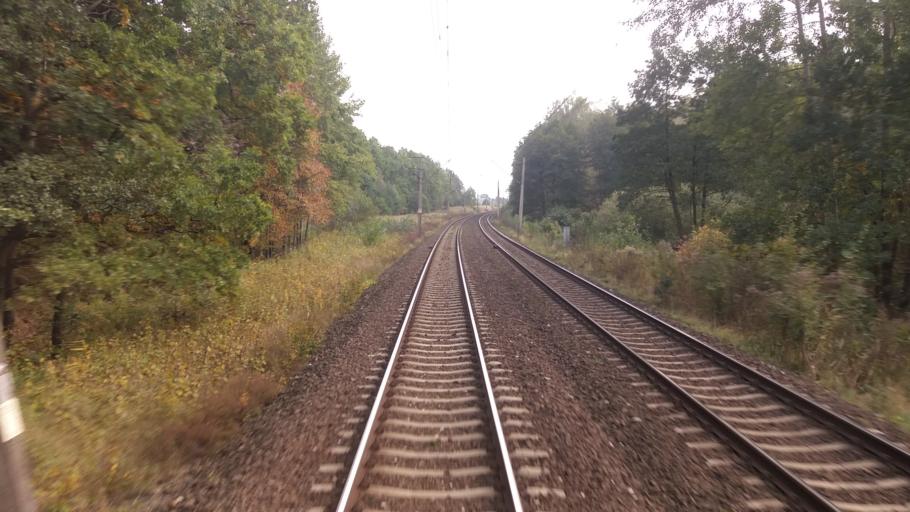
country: PL
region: West Pomeranian Voivodeship
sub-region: Powiat stargardzki
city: Dolice
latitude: 53.2064
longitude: 15.1816
